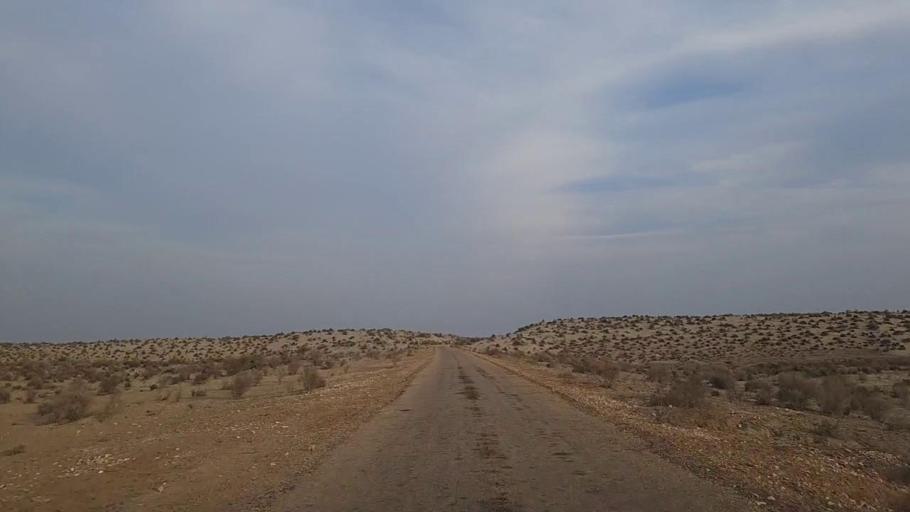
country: PK
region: Sindh
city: Jam Sahib
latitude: 26.4917
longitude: 68.5497
